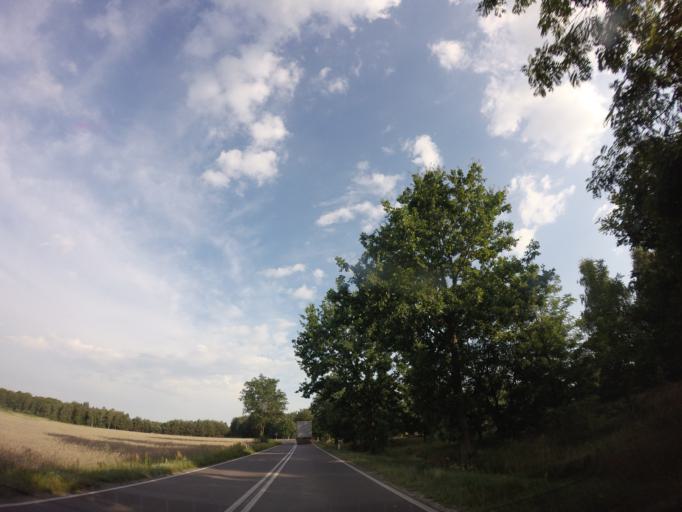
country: PL
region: Lublin Voivodeship
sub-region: Powiat lubartowski
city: Jeziorzany
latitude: 51.5787
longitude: 22.2832
